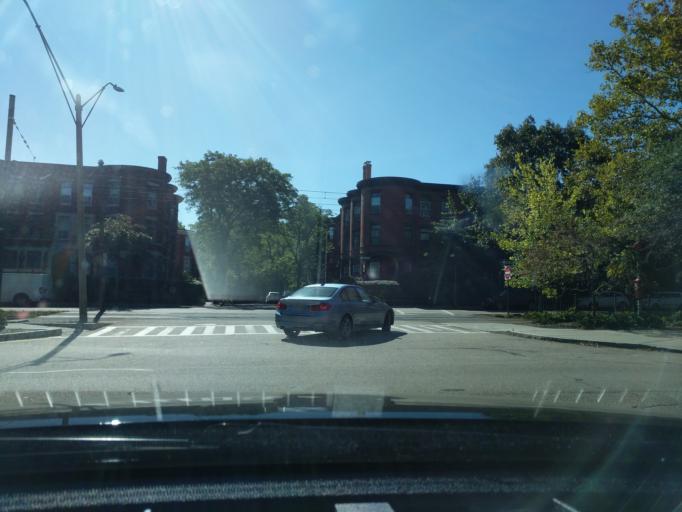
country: US
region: Massachusetts
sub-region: Norfolk County
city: Brookline
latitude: 42.3371
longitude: -71.1472
